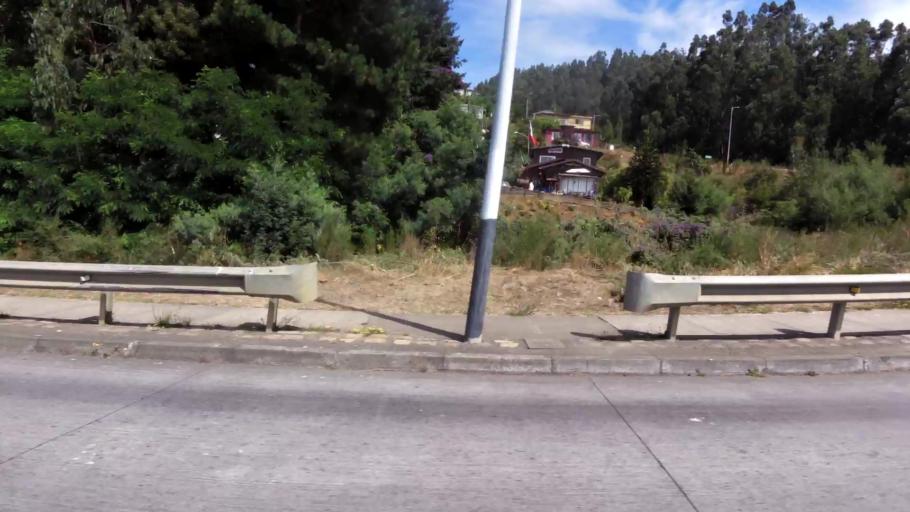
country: CL
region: Biobio
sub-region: Provincia de Concepcion
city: Talcahuano
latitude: -36.7074
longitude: -73.1145
